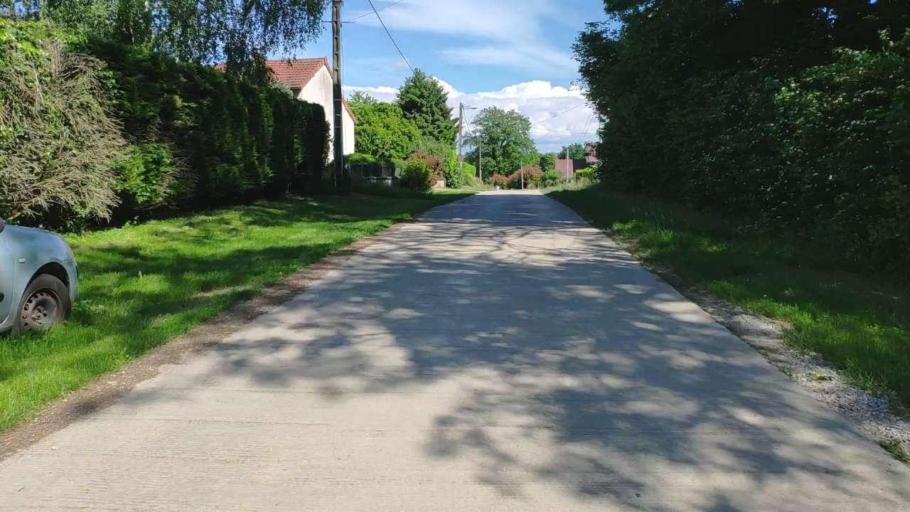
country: FR
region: Franche-Comte
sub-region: Departement du Jura
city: Bletterans
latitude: 46.7670
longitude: 5.4657
